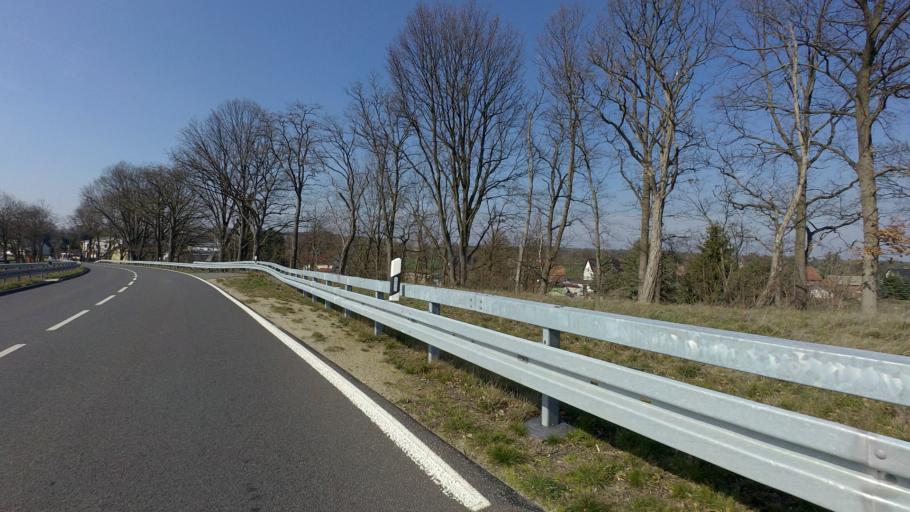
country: DE
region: Brandenburg
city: Drahnsdorf
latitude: 51.9174
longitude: 13.5816
